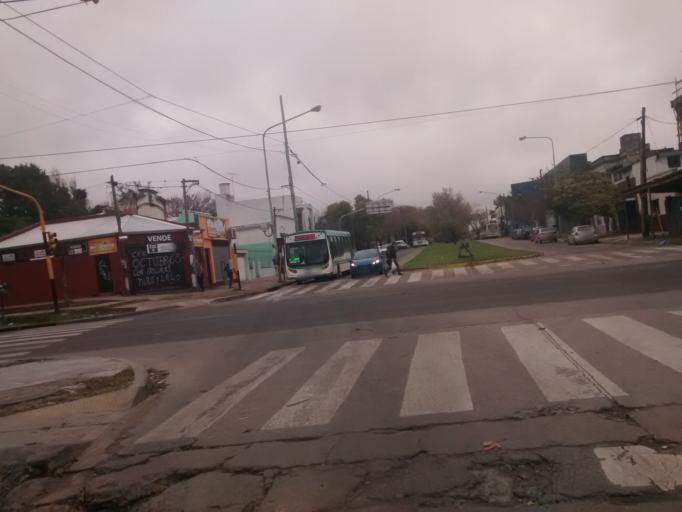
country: AR
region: Buenos Aires
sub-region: Partido de La Plata
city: La Plata
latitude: -34.8920
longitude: -57.9472
